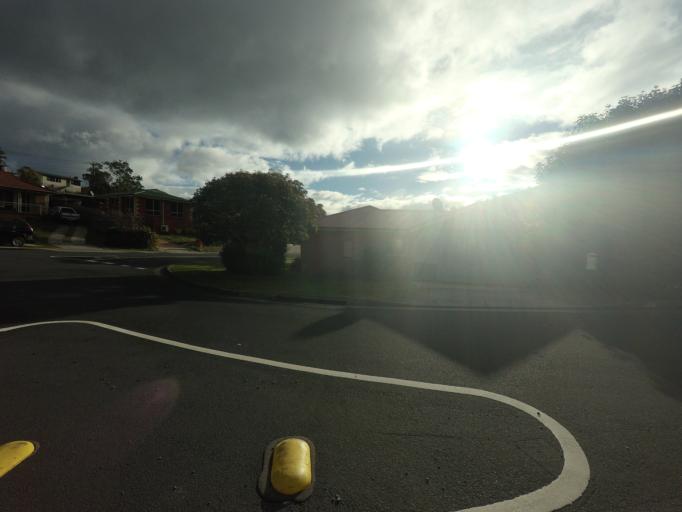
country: AU
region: Tasmania
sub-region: Clarence
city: Warrane
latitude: -42.8566
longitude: 147.4032
